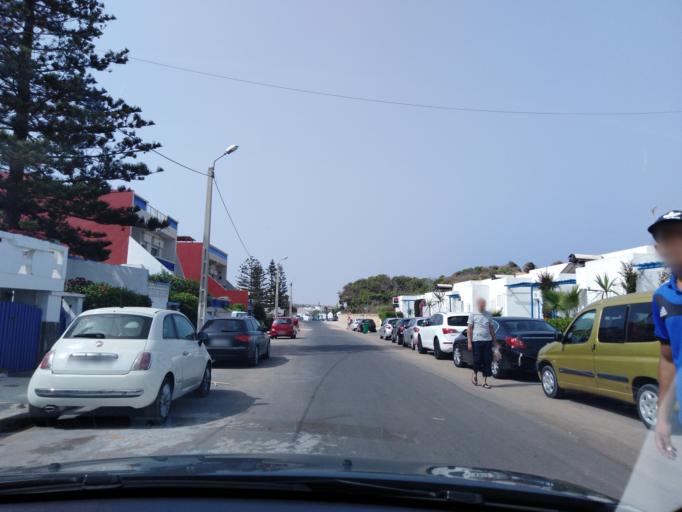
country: MA
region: Doukkala-Abda
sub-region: Safi
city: Safi
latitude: 32.7336
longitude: -9.0453
